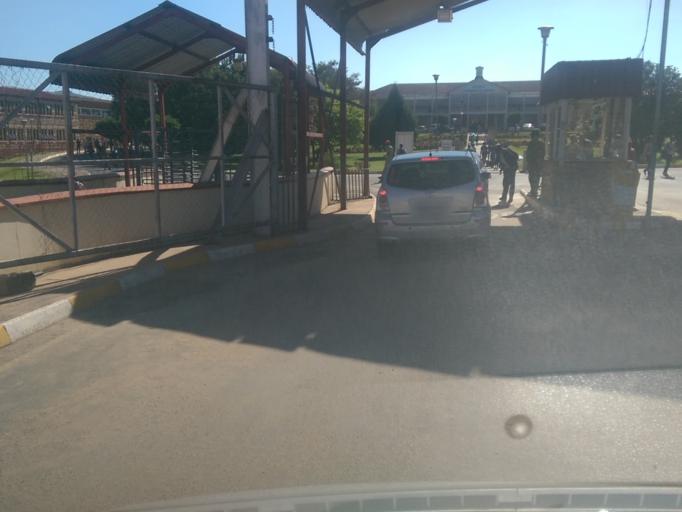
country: LS
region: Maseru
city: Nako
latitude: -29.4512
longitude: 27.7207
